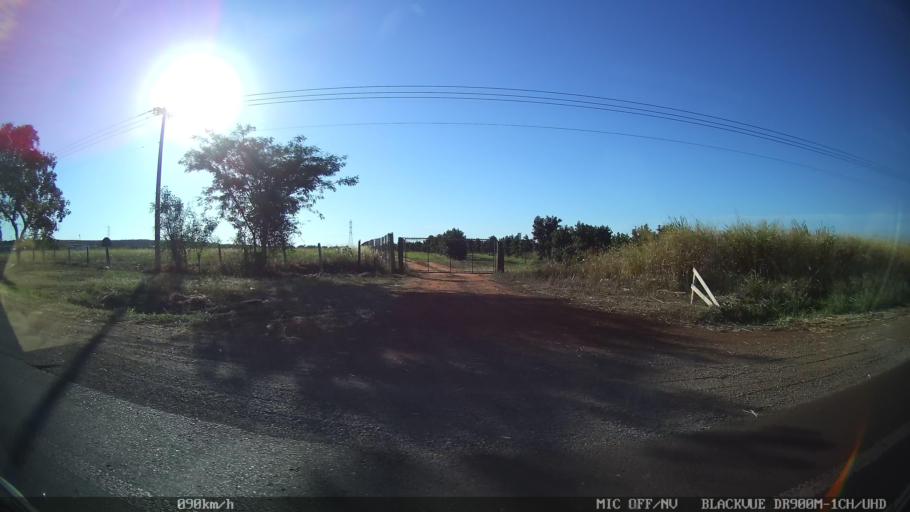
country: BR
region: Sao Paulo
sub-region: Olimpia
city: Olimpia
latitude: -20.7129
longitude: -48.9851
